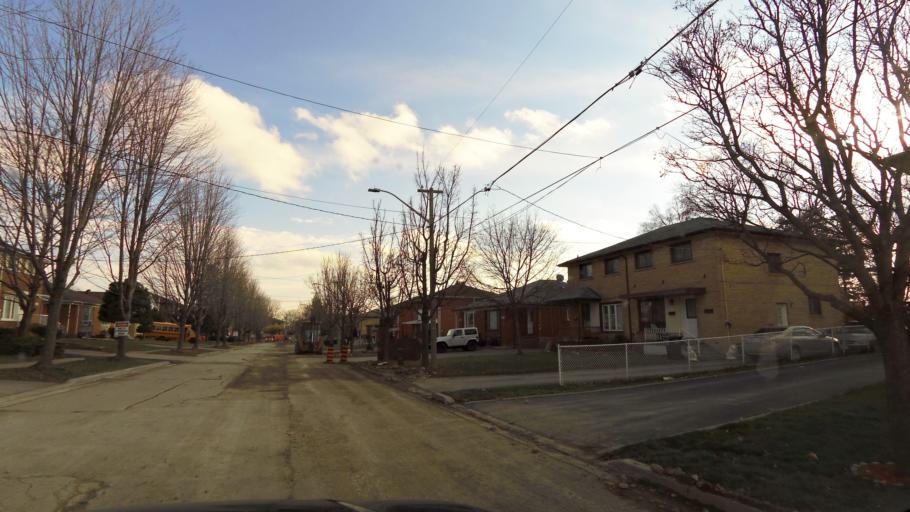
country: CA
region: Ontario
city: Mississauga
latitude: 43.5657
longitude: -79.6648
